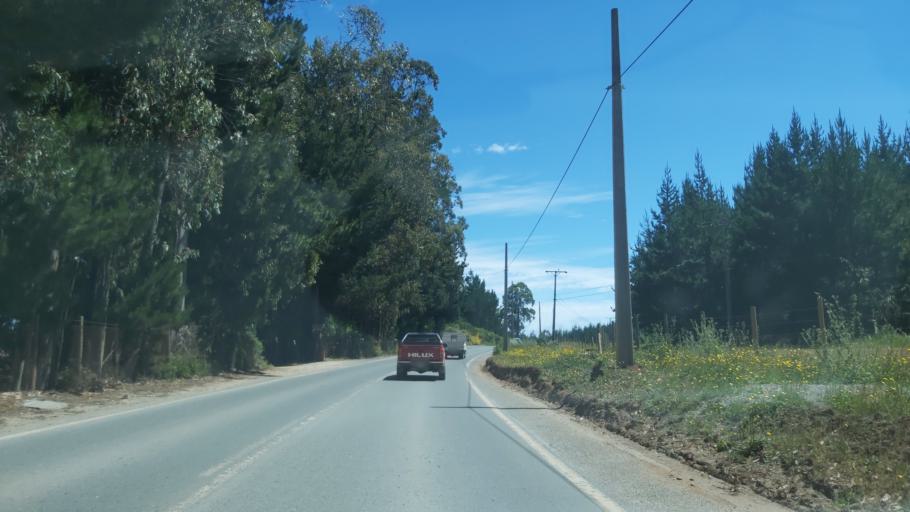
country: CL
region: Maule
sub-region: Provincia de Talca
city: Constitucion
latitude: -35.3969
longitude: -72.4312
